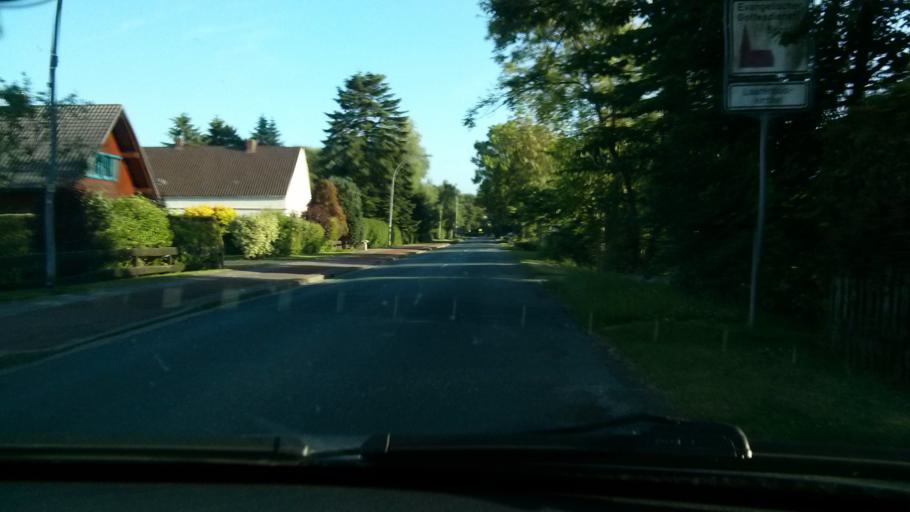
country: DE
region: Lower Saxony
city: Nordenham
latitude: 53.4488
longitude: 8.5023
